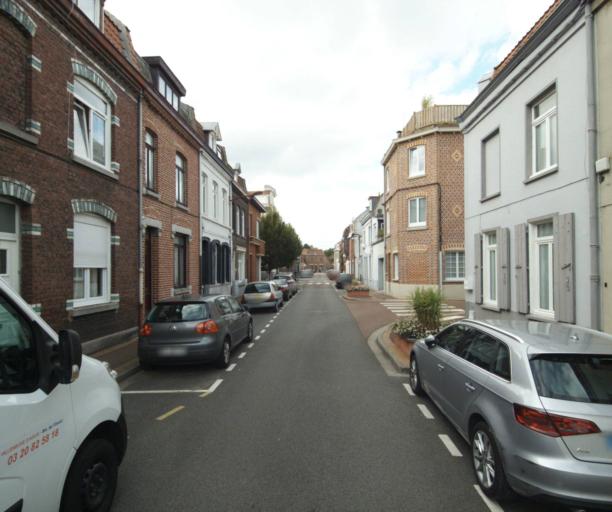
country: FR
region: Nord-Pas-de-Calais
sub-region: Departement du Nord
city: Marcq-en-Baroeul
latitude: 50.6643
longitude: 3.0730
